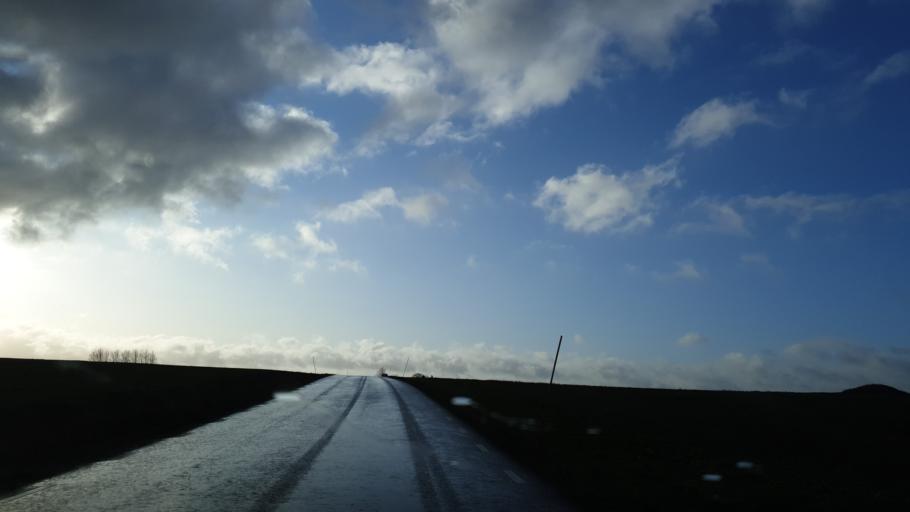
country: SE
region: Skane
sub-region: Skurups Kommun
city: Rydsgard
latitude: 55.4637
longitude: 13.5627
